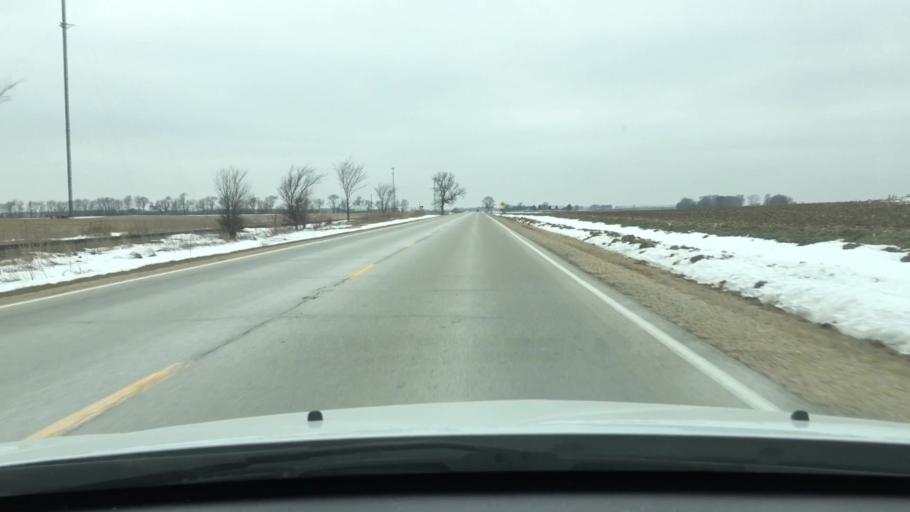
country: US
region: Illinois
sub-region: DeKalb County
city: Waterman
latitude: 41.7692
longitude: -88.8029
